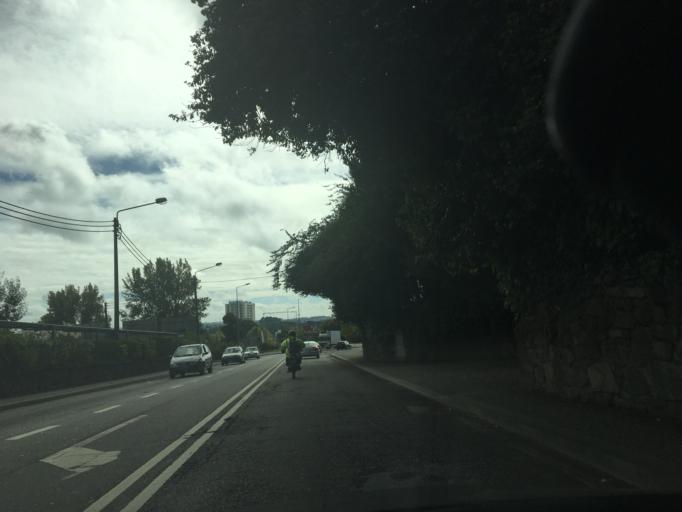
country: PT
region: Porto
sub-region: Maia
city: Gemunde
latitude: 41.2451
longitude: -8.6485
